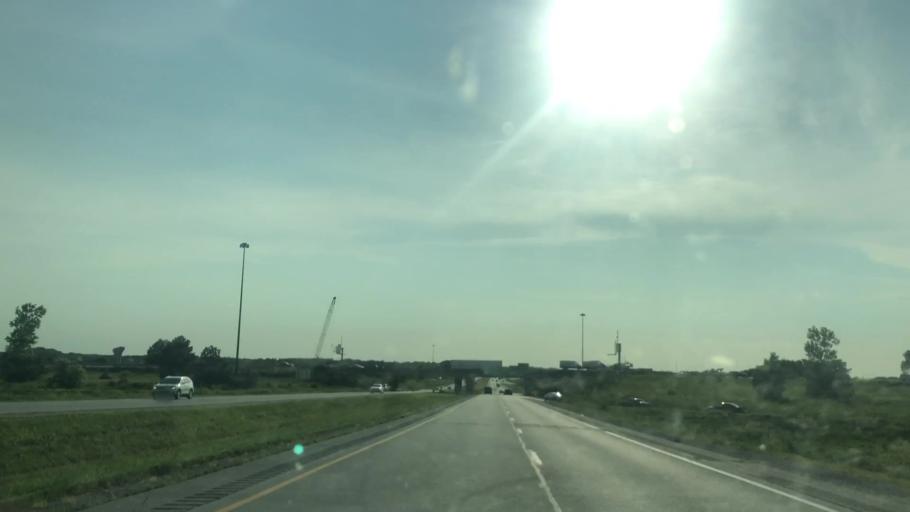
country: US
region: Iowa
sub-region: Story County
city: Ames
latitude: 42.0080
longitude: -93.5681
